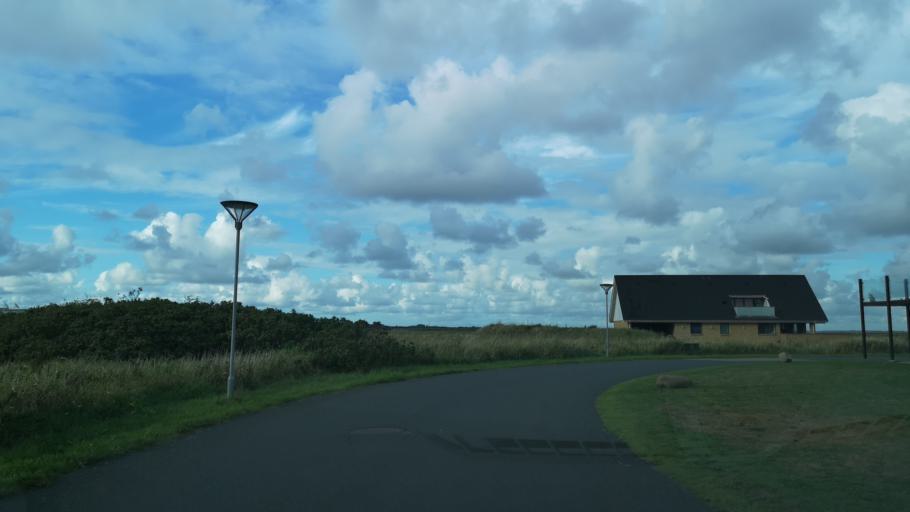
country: DK
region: Central Jutland
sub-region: Ringkobing-Skjern Kommune
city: Hvide Sande
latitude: 56.0241
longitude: 8.1227
